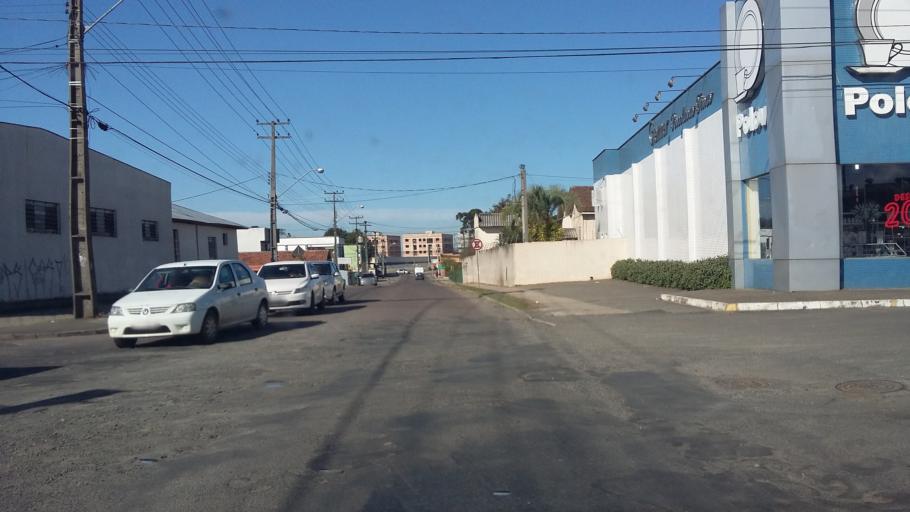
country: BR
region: Parana
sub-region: Campo Largo
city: Campo Largo
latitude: -25.4520
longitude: -49.5418
